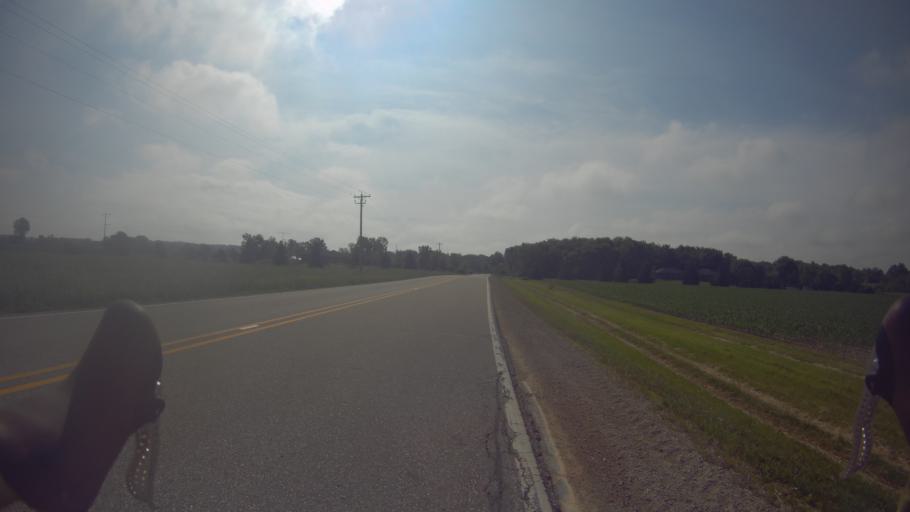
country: US
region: Wisconsin
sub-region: Dane County
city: McFarland
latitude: 43.0146
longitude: -89.2418
